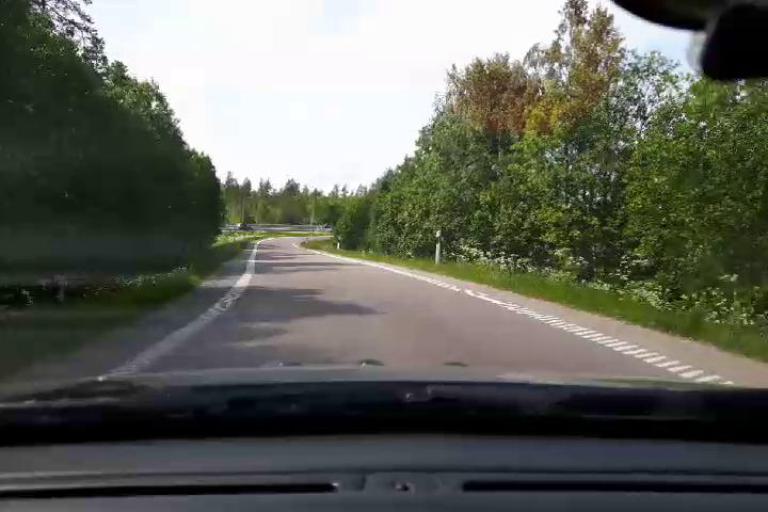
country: SE
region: Gaevleborg
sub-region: Gavle Kommun
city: Gavle
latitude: 60.6505
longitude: 17.1193
